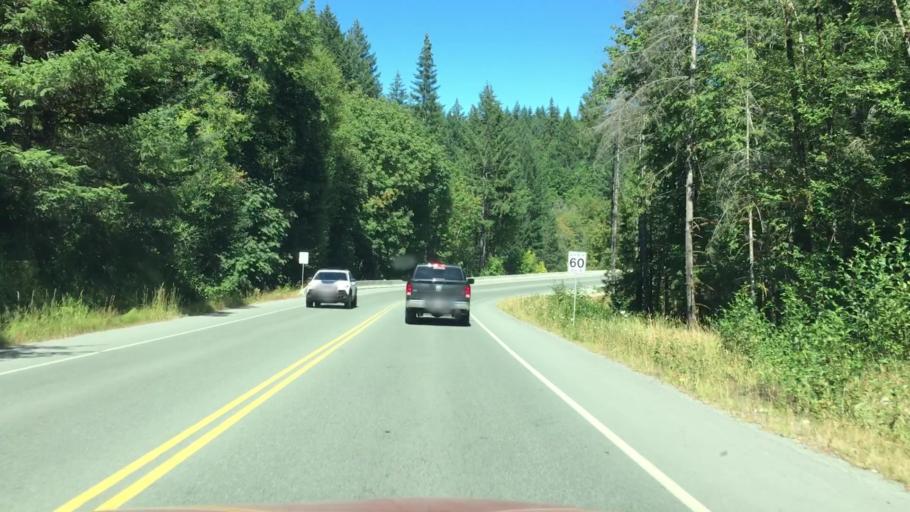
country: CA
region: British Columbia
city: Port Alberni
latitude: 49.2588
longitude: -124.7743
